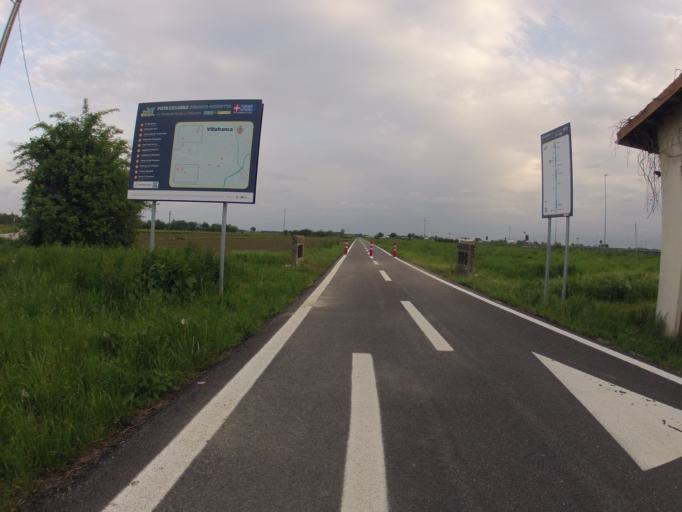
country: IT
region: Piedmont
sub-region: Provincia di Torino
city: Villafranca Piemonte
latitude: 44.8052
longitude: 7.5026
